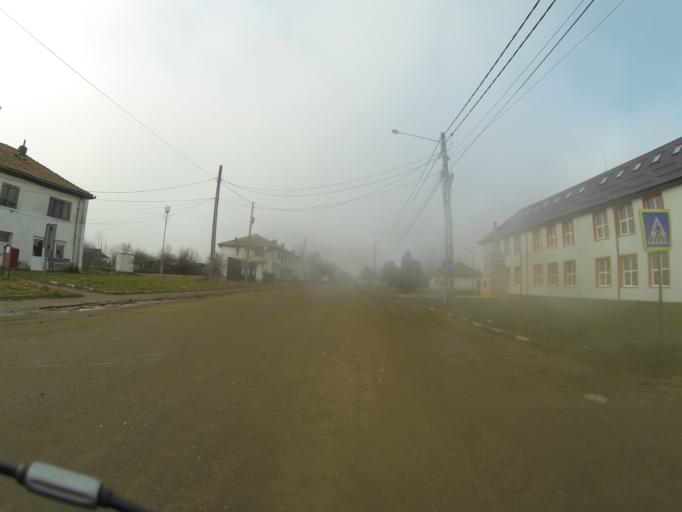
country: RO
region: Mehedinti
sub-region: Comuna Baclesu
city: Baclesu
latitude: 44.4775
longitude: 23.1130
